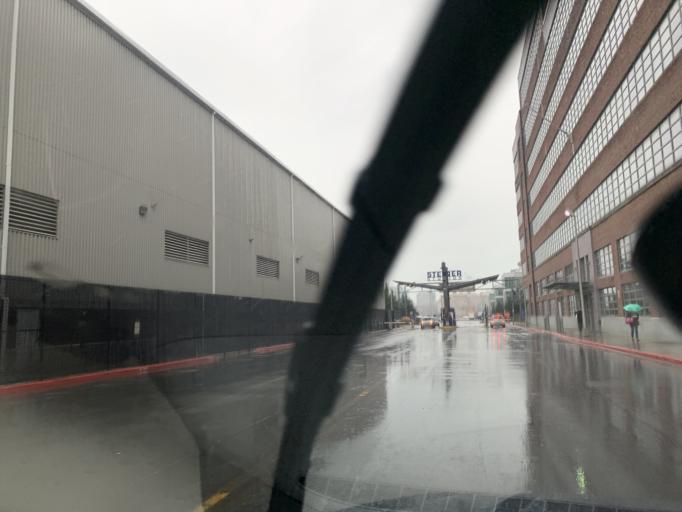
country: US
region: New York
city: New York City
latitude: 40.6981
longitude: -73.9677
